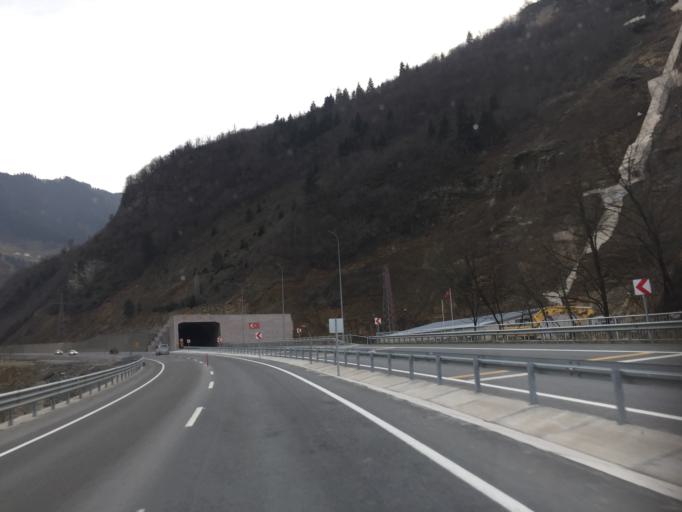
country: TR
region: Trabzon
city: Macka
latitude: 40.7586
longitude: 39.5627
